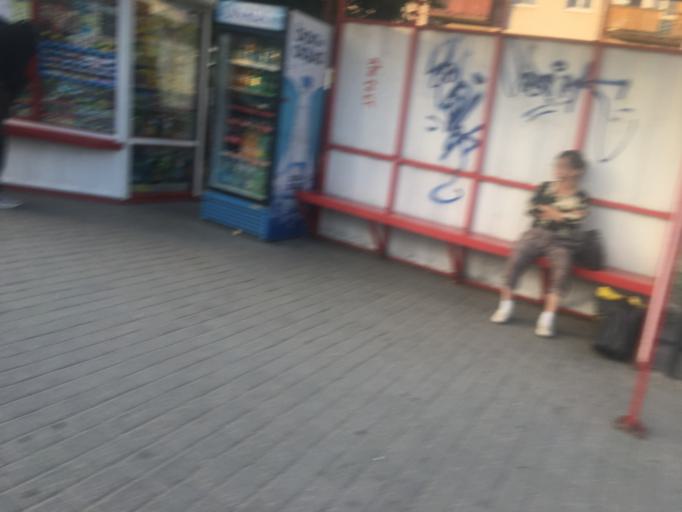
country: BY
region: Grodnenskaya
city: Hrodna
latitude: 53.6973
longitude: 23.8207
